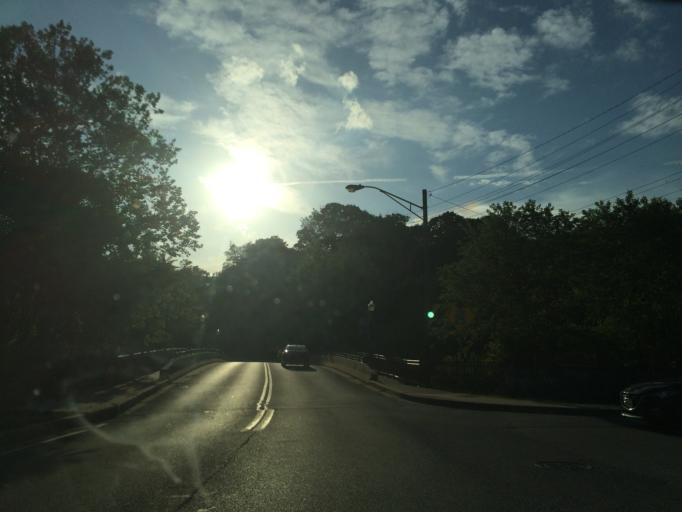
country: US
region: Maryland
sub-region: Howard County
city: Ellicott City
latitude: 39.2676
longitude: -76.7934
